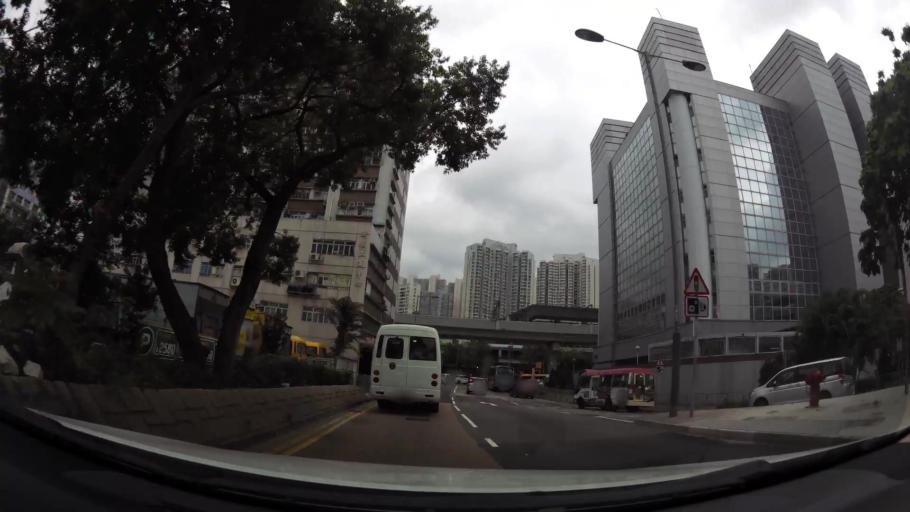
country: HK
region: Kowloon City
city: Kowloon
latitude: 22.3095
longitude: 114.2285
